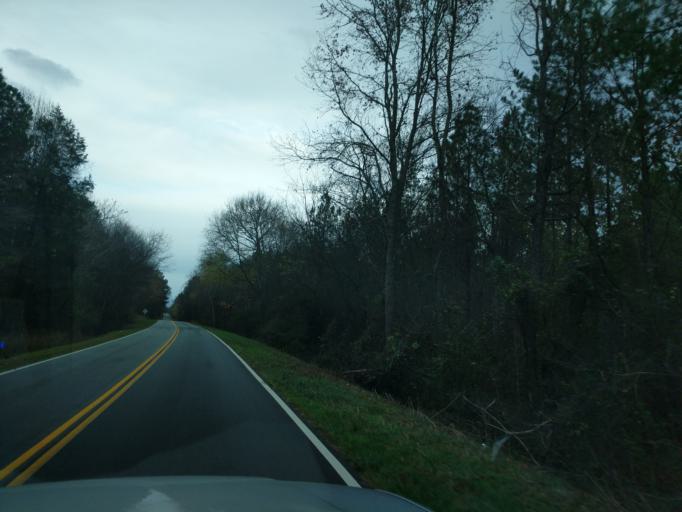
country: US
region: South Carolina
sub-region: Laurens County
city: Laurens
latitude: 34.3818
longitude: -82.0085
